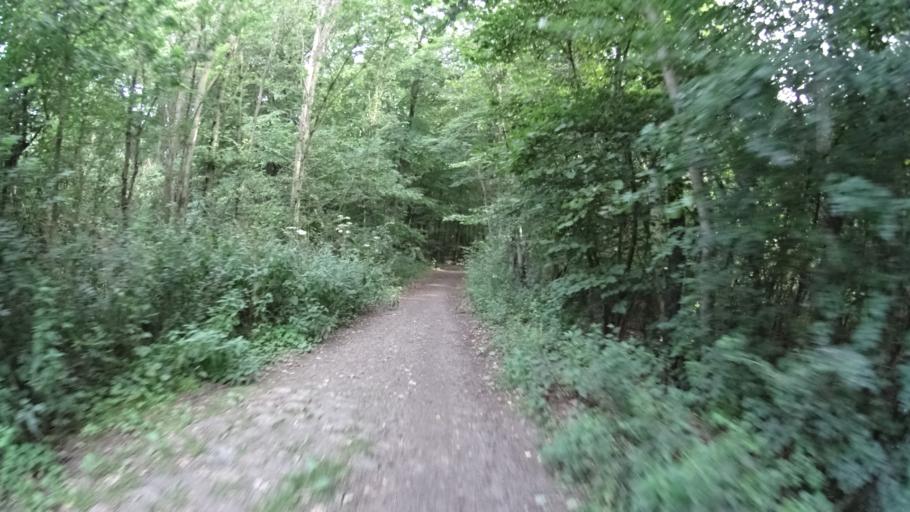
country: DE
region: Lower Saxony
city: Vogelsen
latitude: 53.2788
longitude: 10.3633
